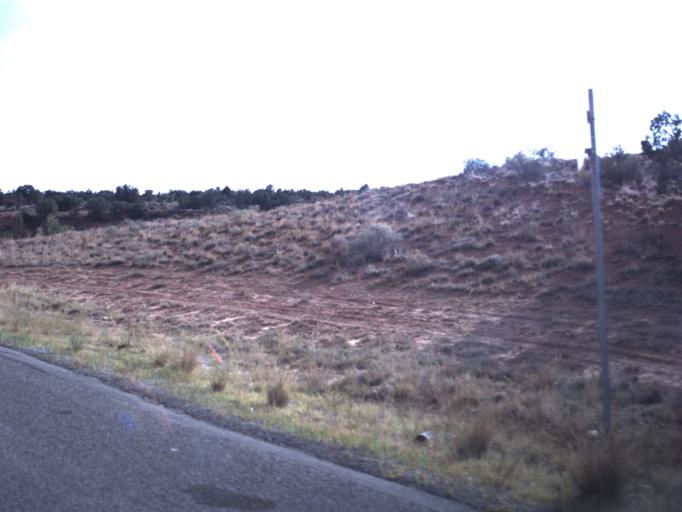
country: US
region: Utah
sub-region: Grand County
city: Moab
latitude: 38.3554
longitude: -109.4347
